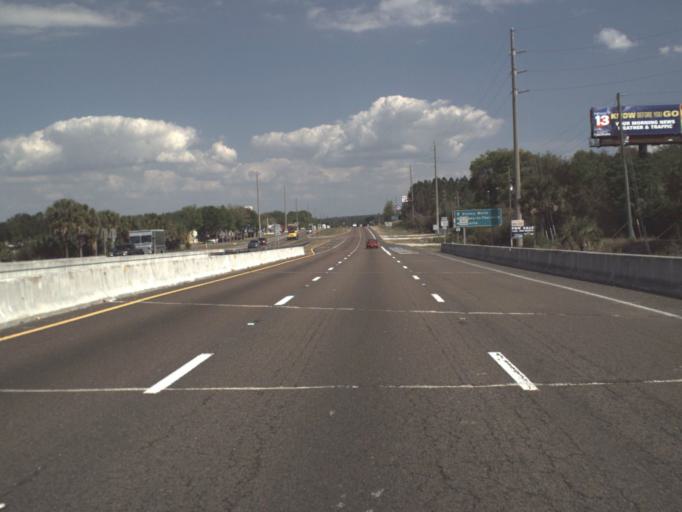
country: US
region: Florida
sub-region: Lake County
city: Howie In The Hills
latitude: 28.6425
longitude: -81.8073
